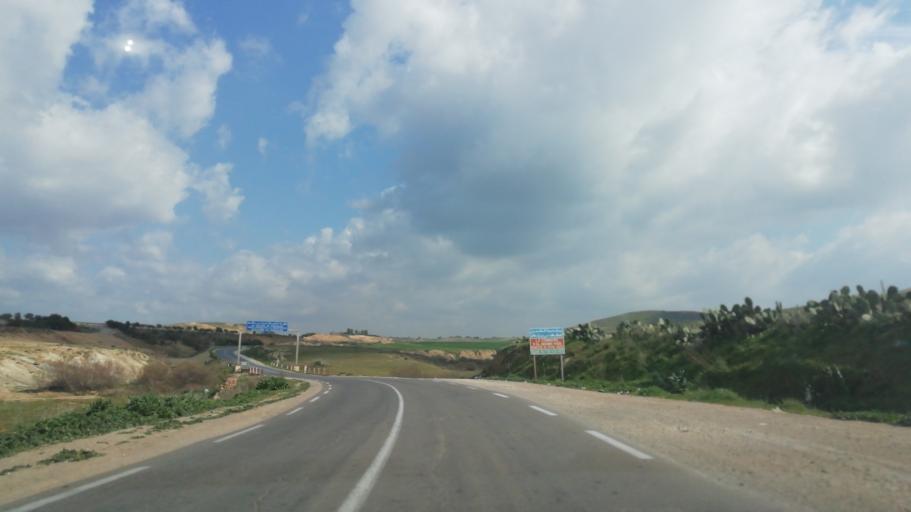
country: DZ
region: Mostaganem
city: Mostaganem
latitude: 35.7017
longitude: 0.2341
